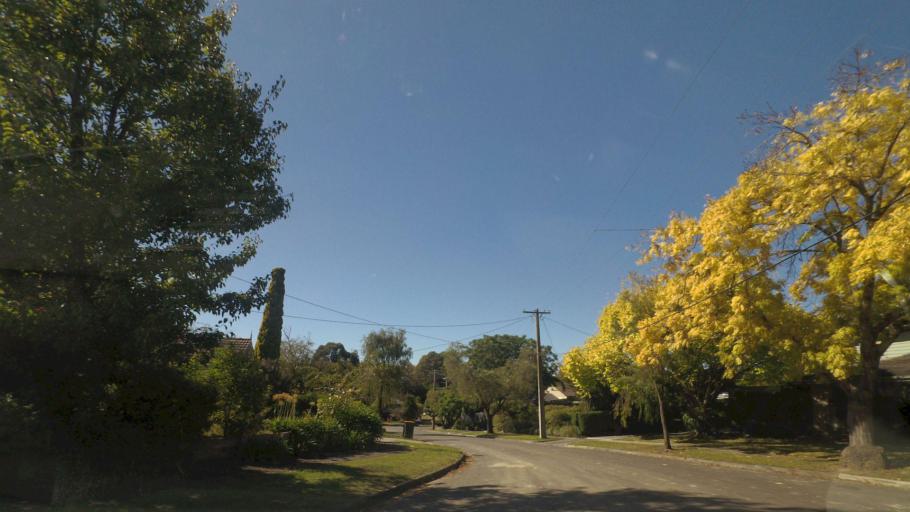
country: AU
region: Victoria
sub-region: Manningham
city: Donvale
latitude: -37.7882
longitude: 145.1685
